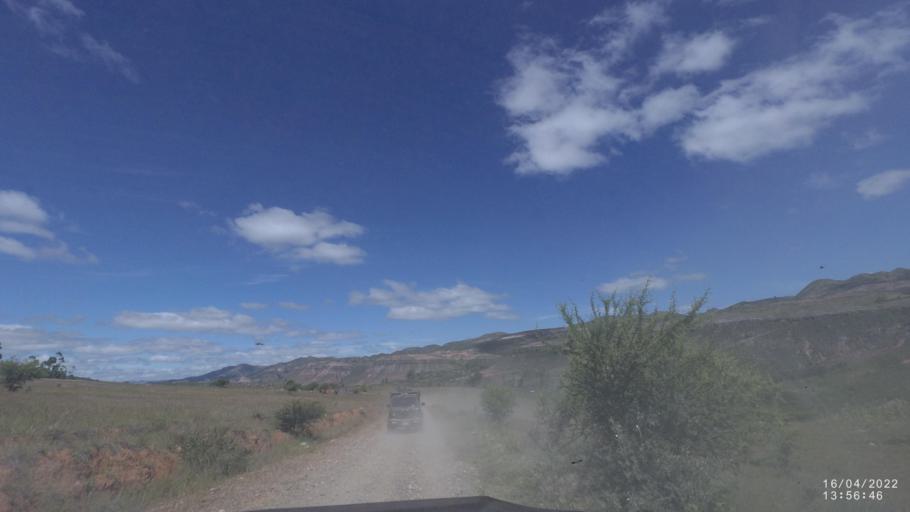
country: BO
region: Cochabamba
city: Mizque
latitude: -18.0336
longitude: -65.5637
